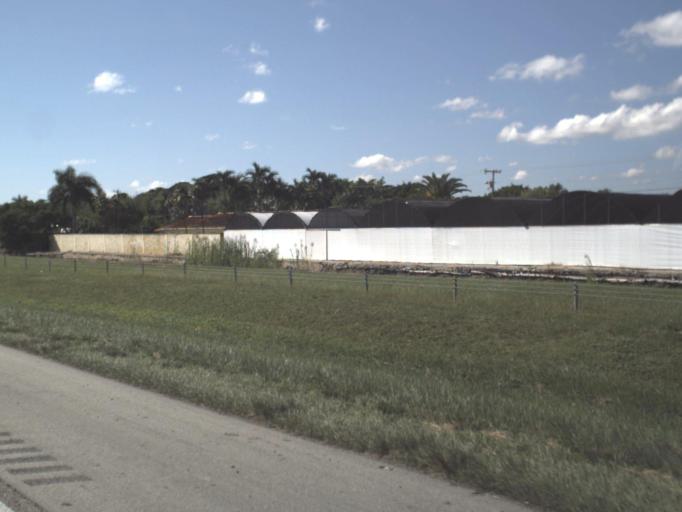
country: US
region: Florida
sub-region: Miami-Dade County
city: Kendale Lakes
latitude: 25.7072
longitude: -80.3836
